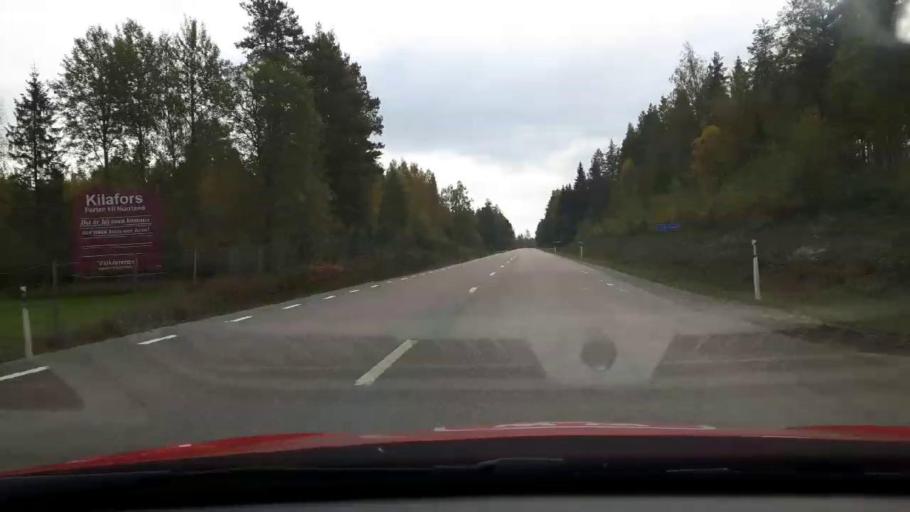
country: SE
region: Gaevleborg
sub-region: Bollnas Kommun
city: Kilafors
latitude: 61.2819
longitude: 16.5197
